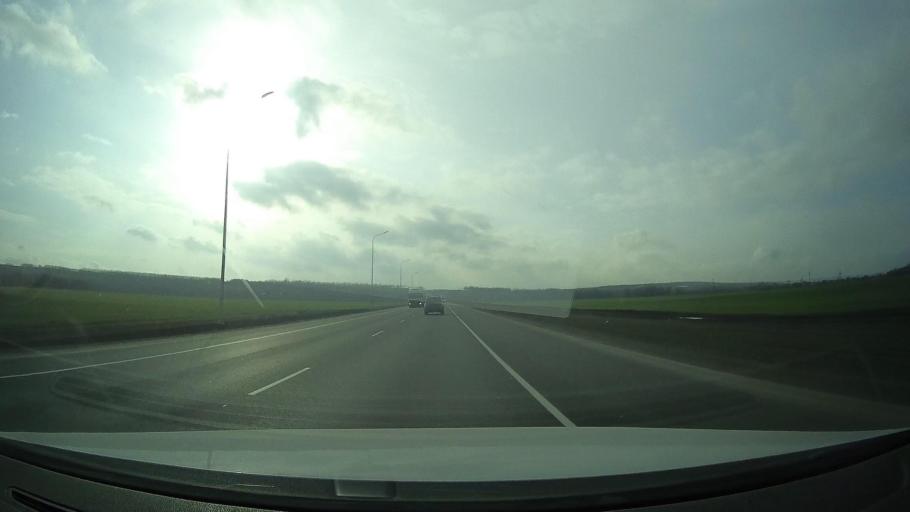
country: RU
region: Rostov
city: Grushevskaya
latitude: 47.4435
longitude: 39.8757
